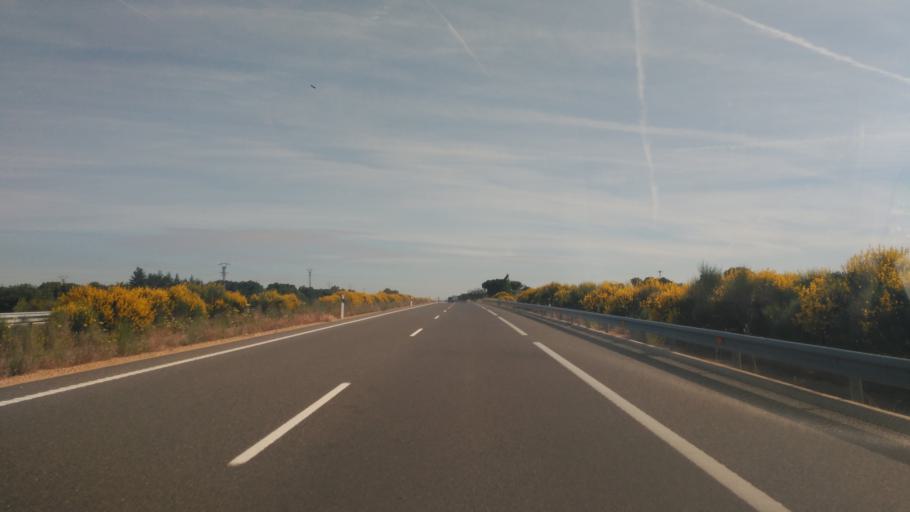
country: ES
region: Castille and Leon
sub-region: Provincia de Salamanca
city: Calzada de Valdunciel
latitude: 41.1395
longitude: -5.6965
